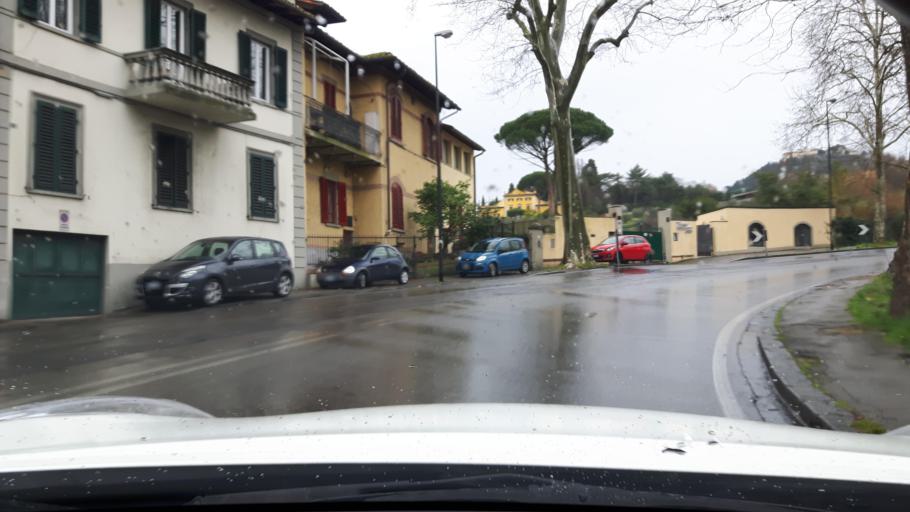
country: IT
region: Tuscany
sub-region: Province of Florence
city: Fiesole
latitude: 43.7954
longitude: 11.2839
